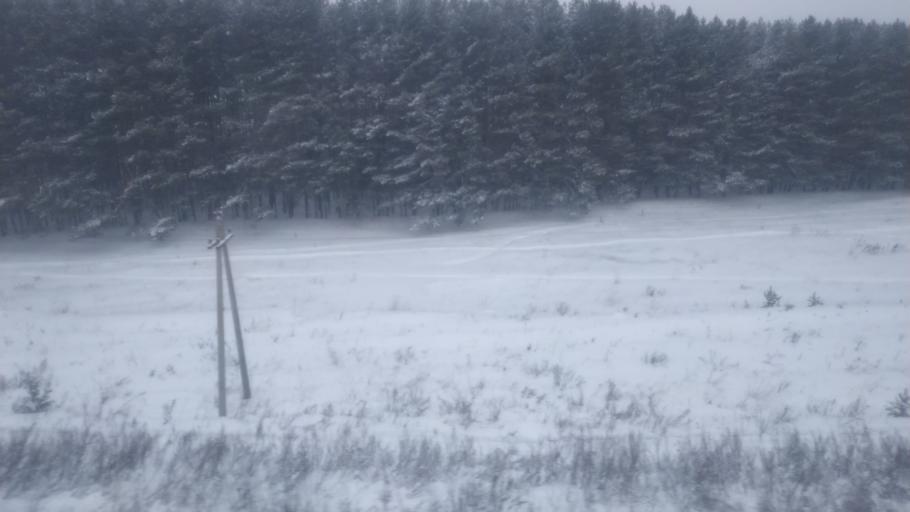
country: RU
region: Udmurtiya
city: Kiyasovo
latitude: 56.5031
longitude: 53.2160
